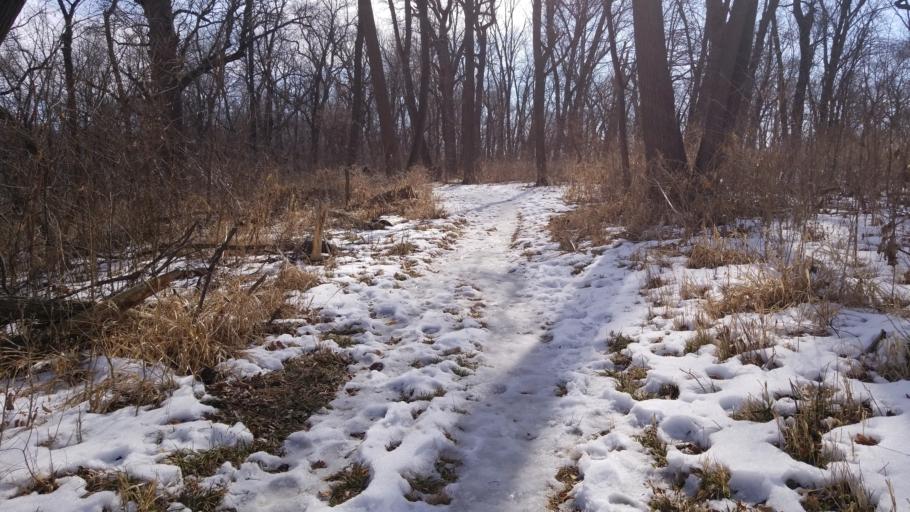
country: US
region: Nebraska
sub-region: Sarpy County
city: Bellevue
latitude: 41.1760
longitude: -95.9020
